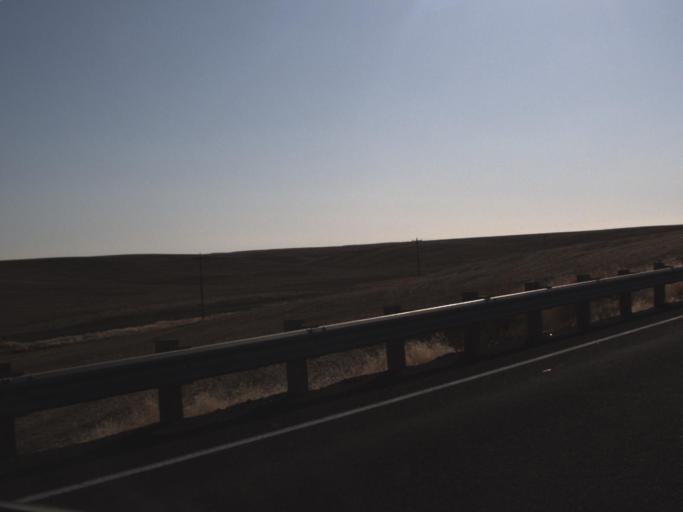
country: US
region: Washington
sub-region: Walla Walla County
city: Garrett
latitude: 46.2896
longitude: -118.5449
